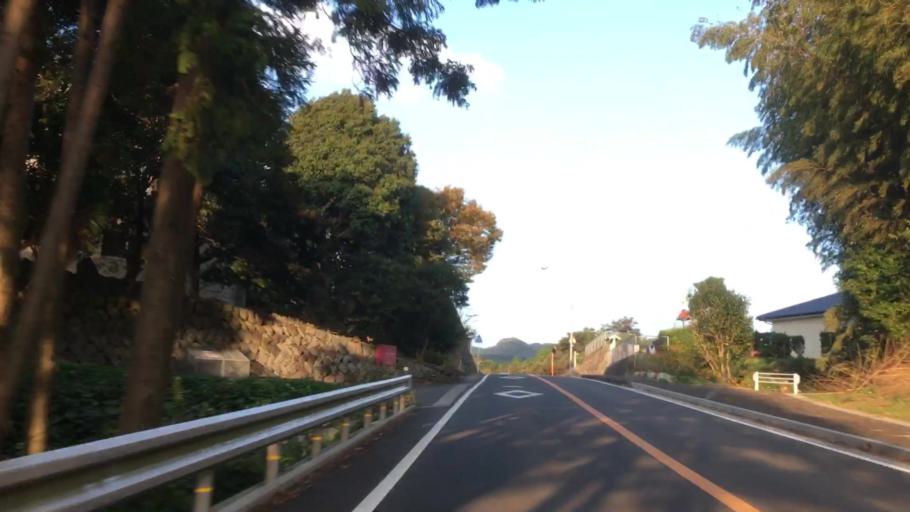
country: JP
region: Nagasaki
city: Sasebo
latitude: 33.0377
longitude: 129.6692
